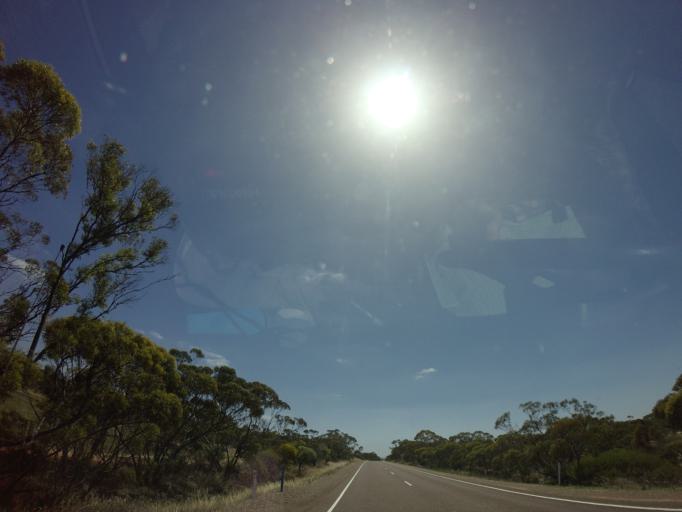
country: AU
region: South Australia
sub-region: Kimba
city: Caralue
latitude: -33.2238
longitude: 136.3339
